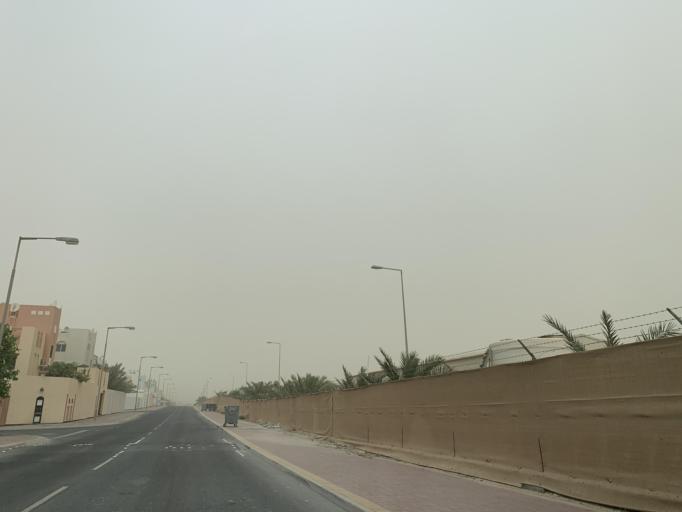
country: BH
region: Central Governorate
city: Madinat Hamad
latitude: 26.1250
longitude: 50.5094
